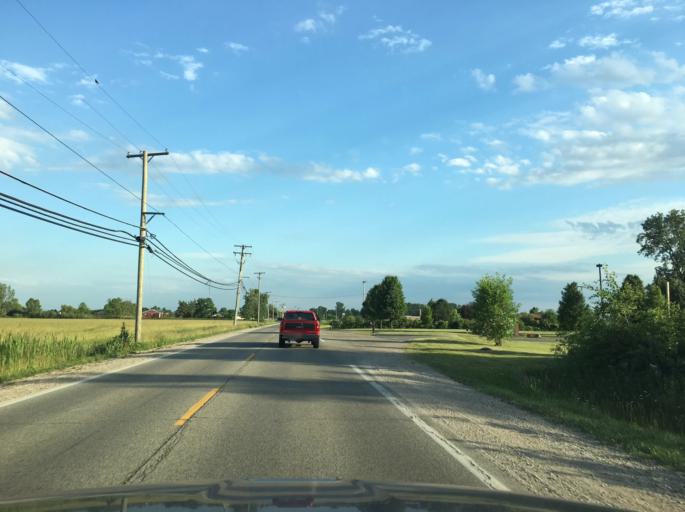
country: US
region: Michigan
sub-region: Macomb County
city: Shelby
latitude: 42.7206
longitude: -82.9597
